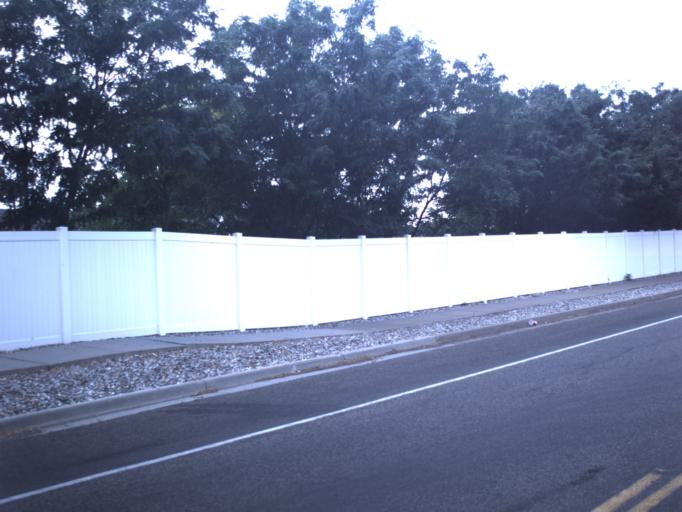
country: US
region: Utah
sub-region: Davis County
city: Farmington
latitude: 40.9680
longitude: -111.8834
